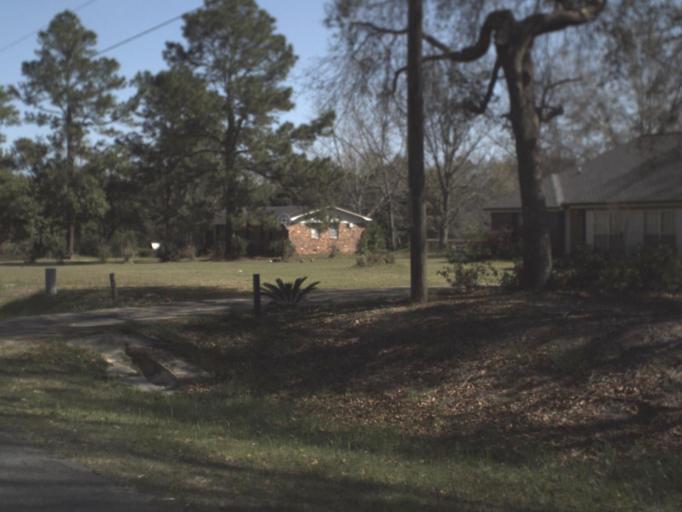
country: US
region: Florida
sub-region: Jefferson County
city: Monticello
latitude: 30.5100
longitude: -84.0243
